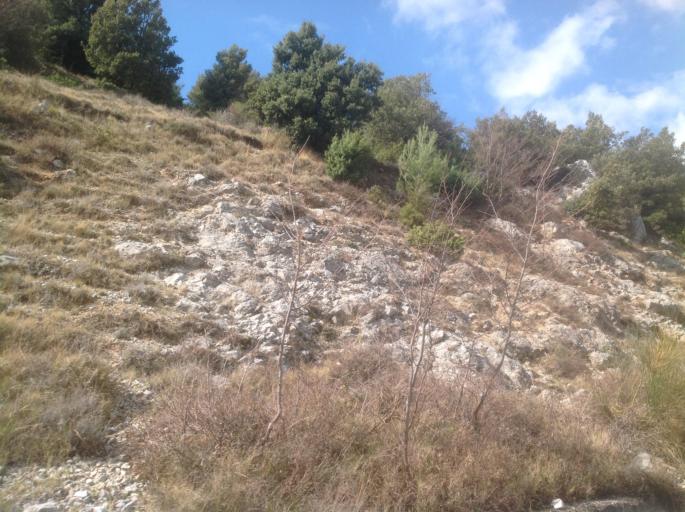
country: IT
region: Calabria
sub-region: Provincia di Cosenza
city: Civita
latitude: 39.8290
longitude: 16.3043
